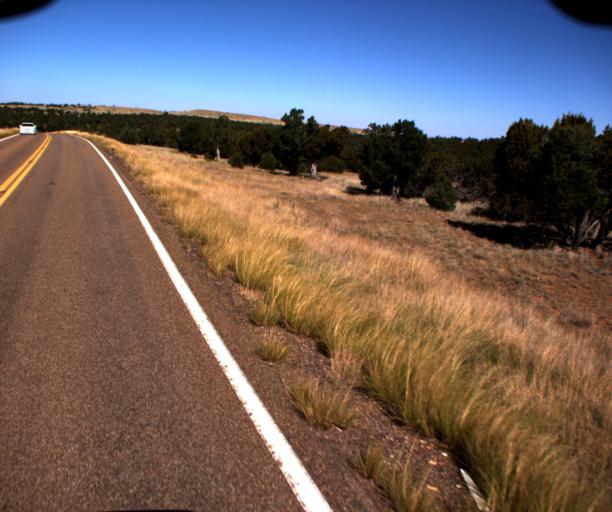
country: US
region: Arizona
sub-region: Navajo County
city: Heber-Overgaard
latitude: 34.4569
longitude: -110.4650
